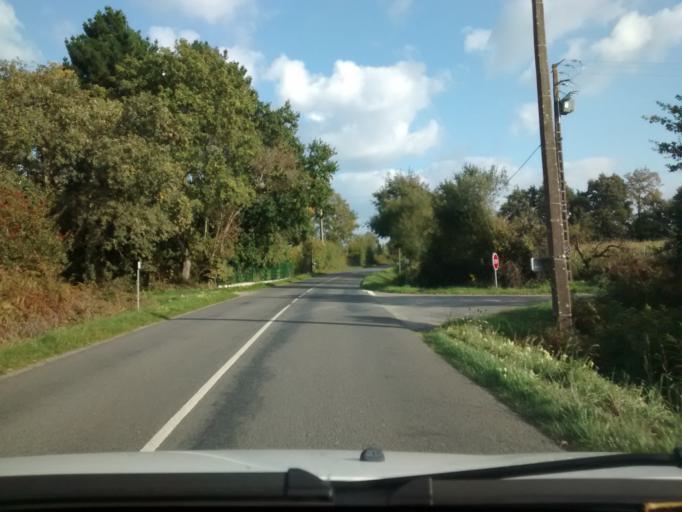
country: FR
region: Pays de la Loire
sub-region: Departement de la Loire-Atlantique
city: Orvault
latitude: 47.2821
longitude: -1.6461
